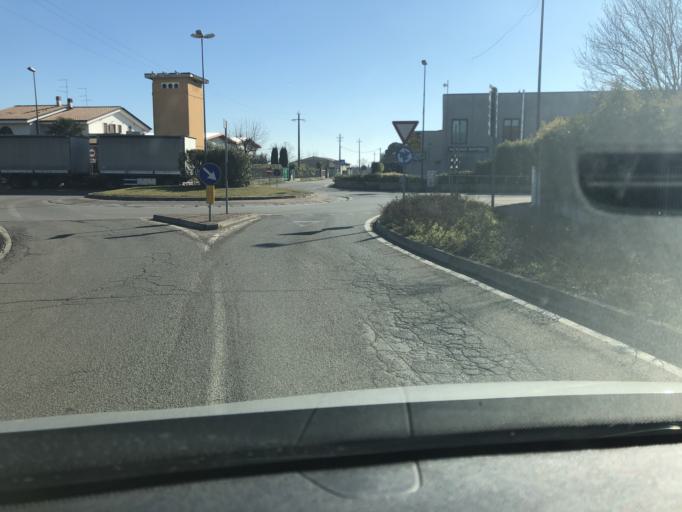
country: IT
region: Veneto
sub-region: Provincia di Verona
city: Lugagnano
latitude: 45.4329
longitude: 10.8698
